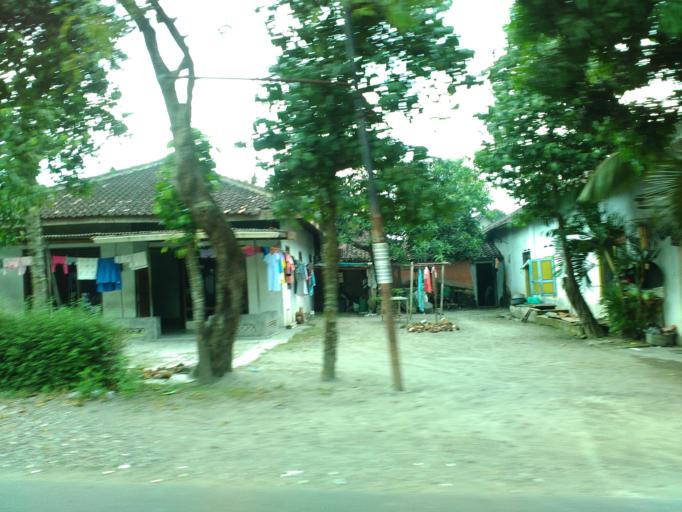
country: ID
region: Central Java
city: Ceper
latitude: -7.6626
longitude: 110.6608
